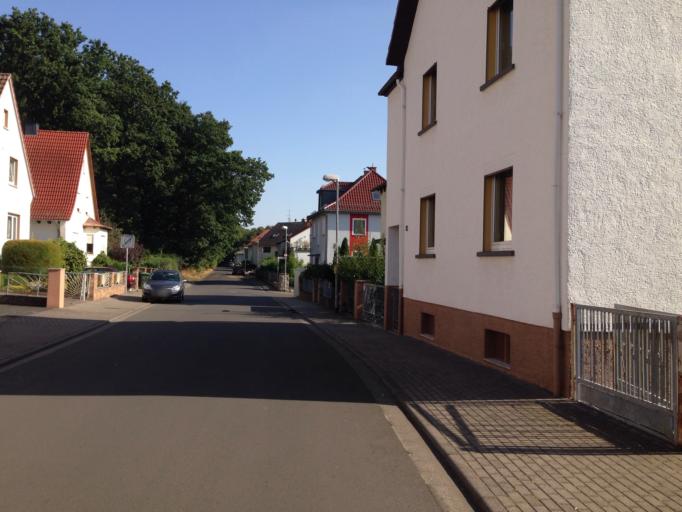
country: DE
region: Hesse
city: Staufenberg
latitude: 50.6476
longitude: 8.7396
